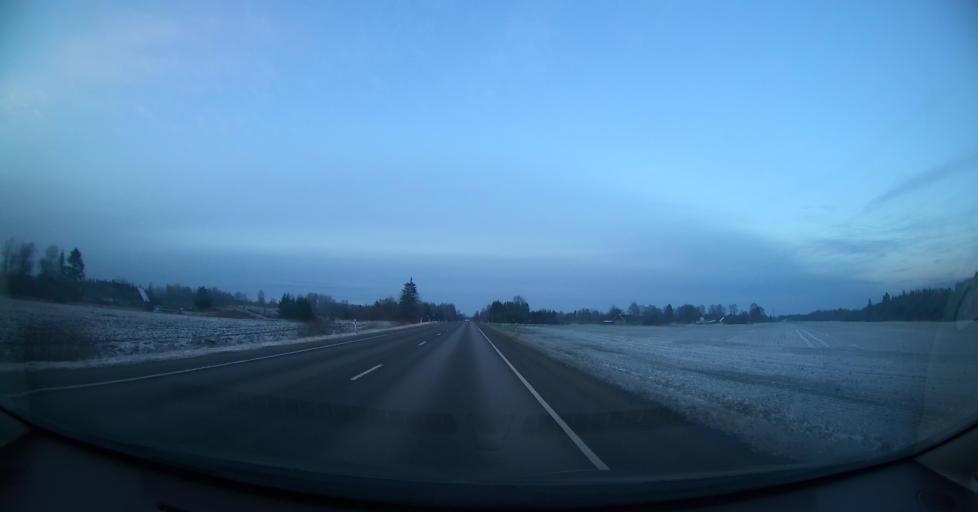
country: EE
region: Jaervamaa
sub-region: Paide linn
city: Paide
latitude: 58.8033
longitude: 25.7582
